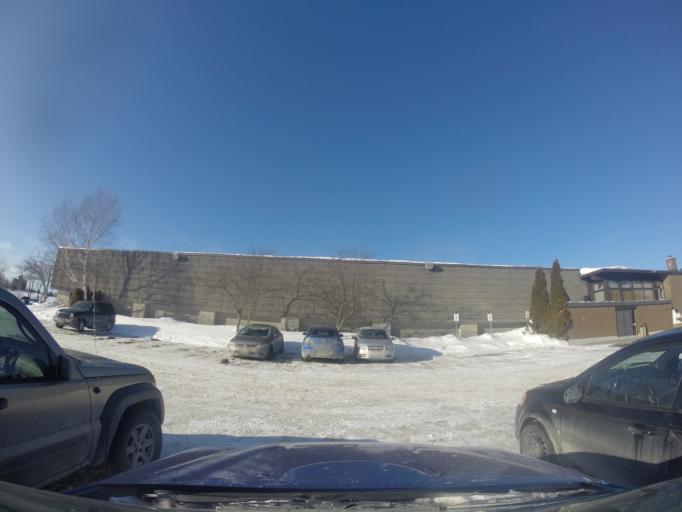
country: CA
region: Ontario
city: Greater Sudbury
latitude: 46.4645
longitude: -80.9867
